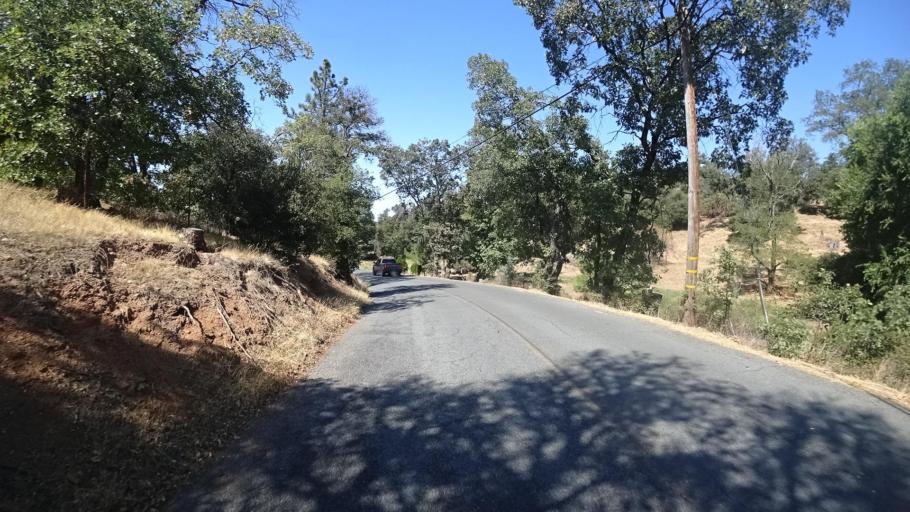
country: US
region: California
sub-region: San Diego County
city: Julian
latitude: 33.0745
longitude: -116.5843
